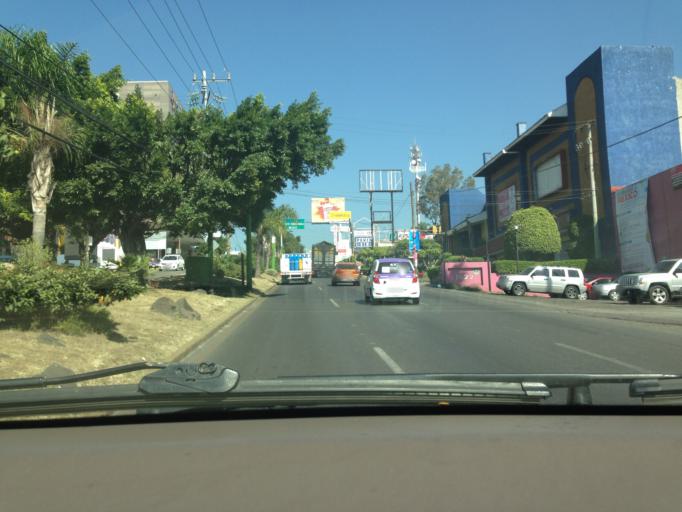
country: MX
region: Morelos
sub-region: Cuernavaca
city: Fraccionamiento Lomas de Ahuatlan
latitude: 18.9539
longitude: -99.2363
